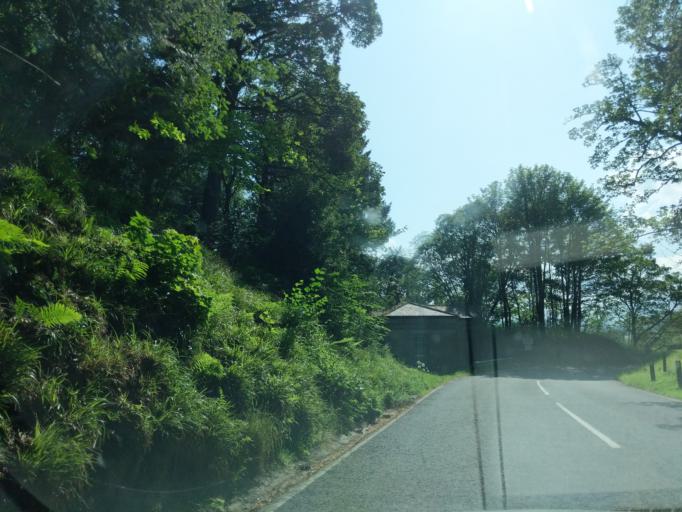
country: GB
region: Scotland
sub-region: Moray
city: Rothes
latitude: 57.5507
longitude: -3.1393
